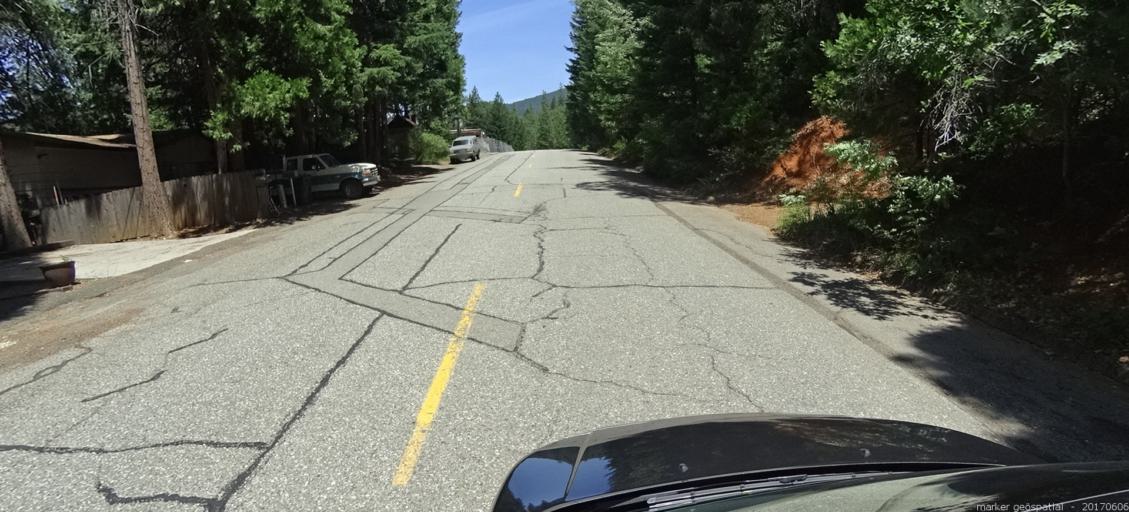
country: US
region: California
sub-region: Siskiyou County
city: Dunsmuir
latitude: 41.2322
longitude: -122.2723
